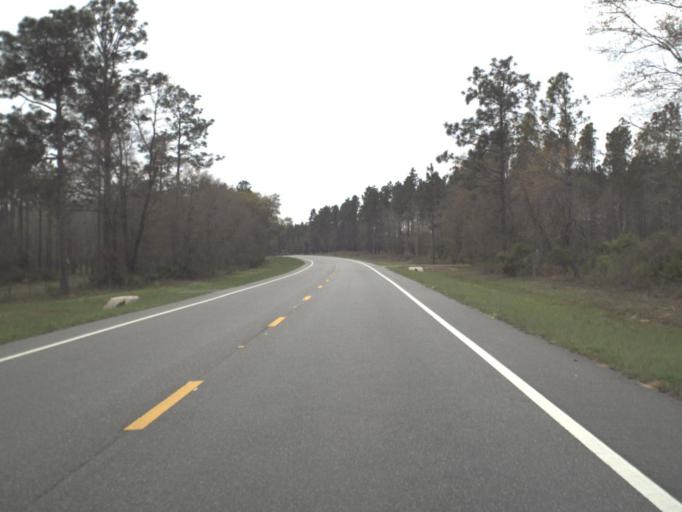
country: US
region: Florida
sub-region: Calhoun County
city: Blountstown
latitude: 30.3799
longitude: -85.2154
